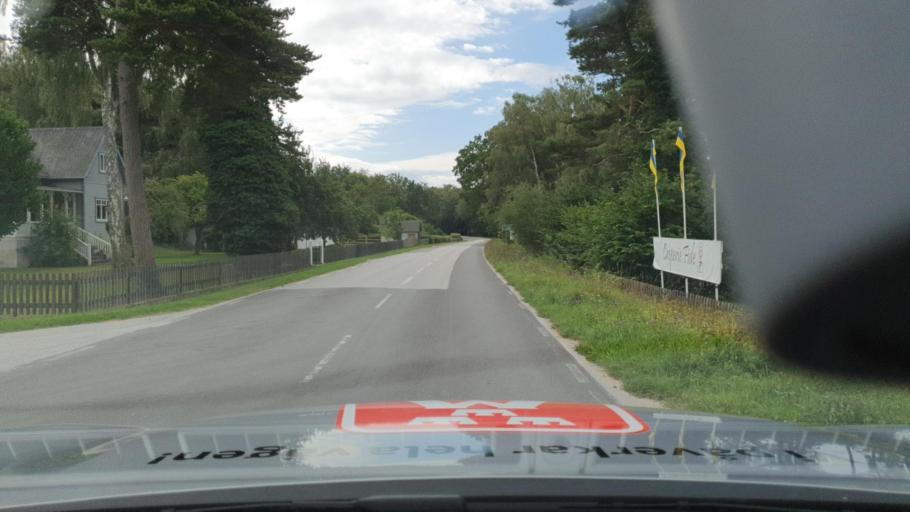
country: SE
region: Gotland
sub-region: Gotland
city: Hemse
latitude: 57.0941
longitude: 18.3039
